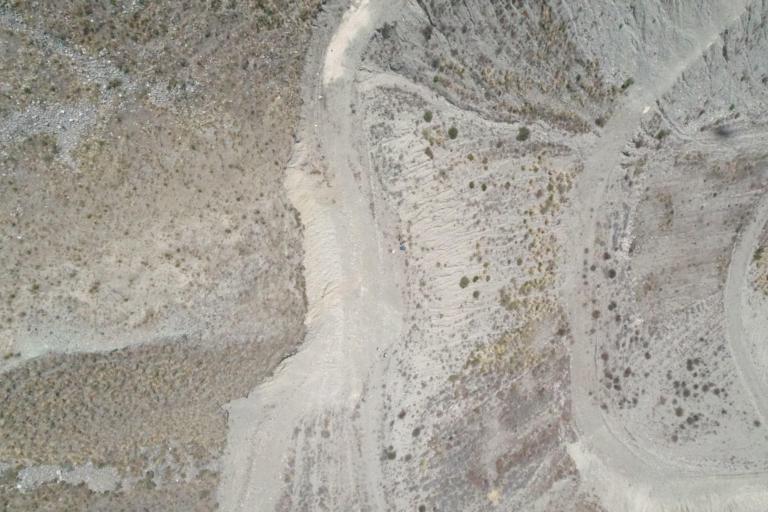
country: BO
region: La Paz
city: La Paz
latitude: -16.4723
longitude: -68.0982
